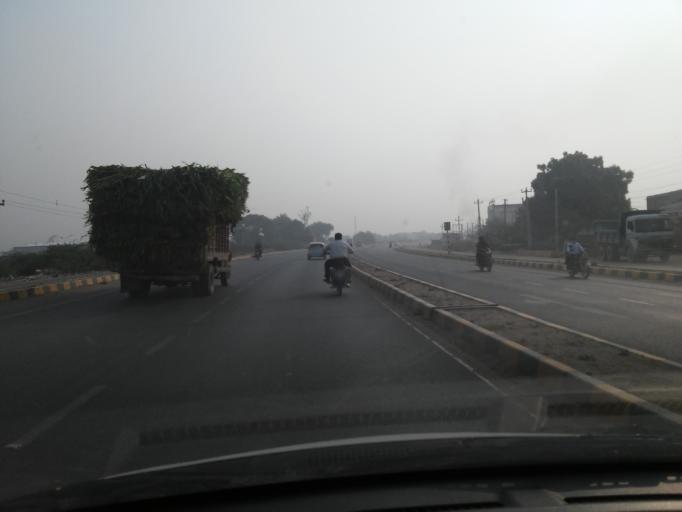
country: IN
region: Gujarat
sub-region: Kachchh
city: Bhuj
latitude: 23.2399
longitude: 69.7159
